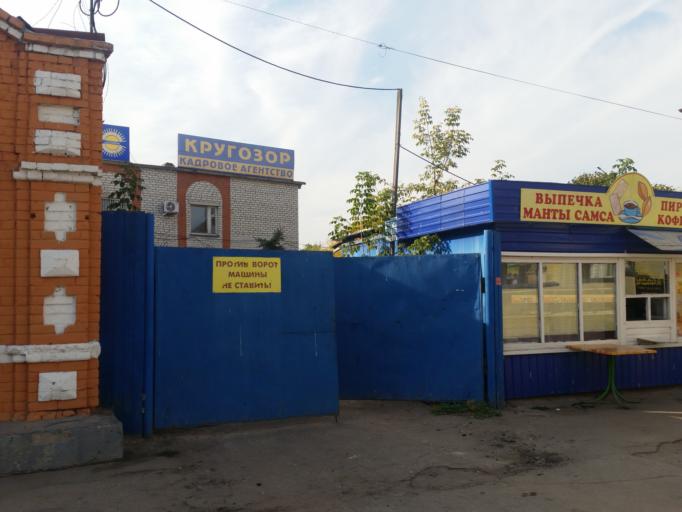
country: RU
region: Ulyanovsk
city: Dimitrovgrad
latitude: 54.2160
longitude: 49.6211
